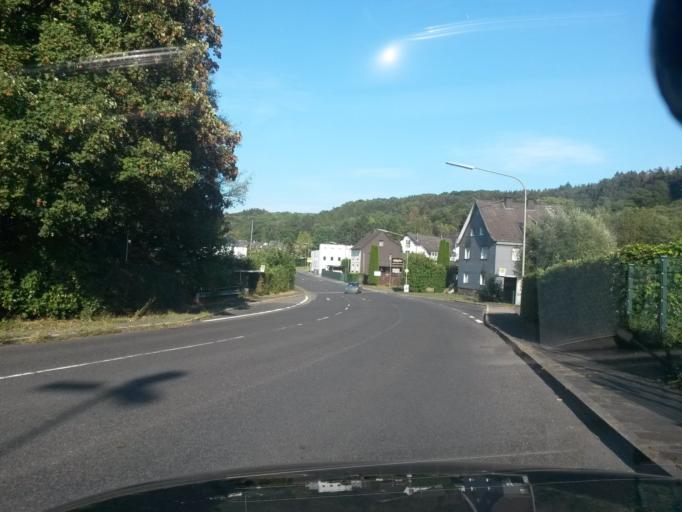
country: DE
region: North Rhine-Westphalia
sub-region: Regierungsbezirk Koln
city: Numbrecht
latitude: 50.9119
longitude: 7.5252
